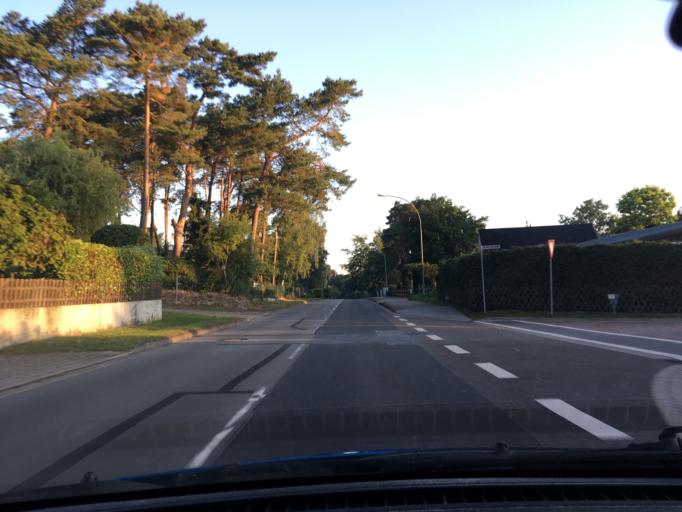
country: DE
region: Lower Saxony
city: Harmstorf
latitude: 53.3805
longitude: 10.0303
